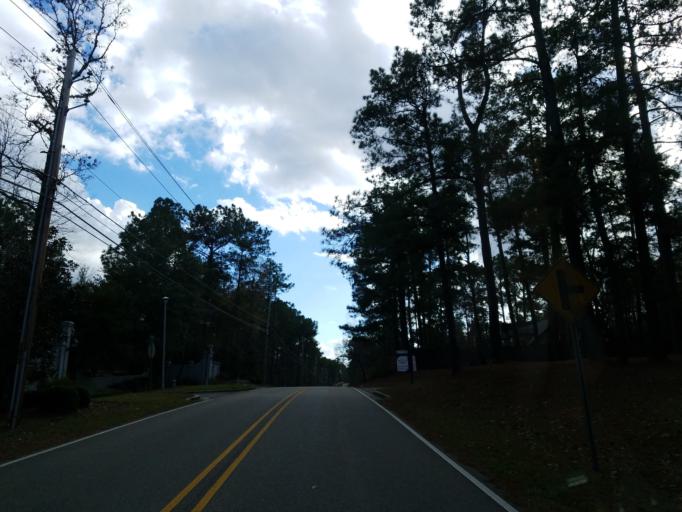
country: US
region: Mississippi
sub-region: Lamar County
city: West Hattiesburg
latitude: 31.2918
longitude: -89.3478
